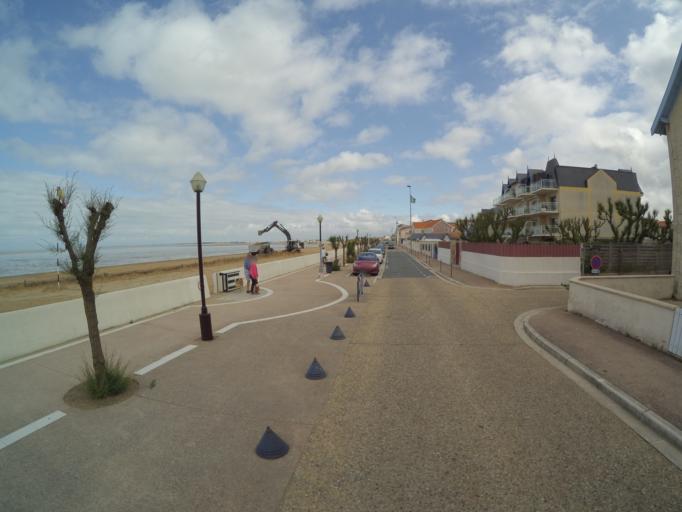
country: FR
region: Poitou-Charentes
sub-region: Departement de la Charente-Maritime
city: Chatelaillon-Plage
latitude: 46.0732
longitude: -1.0932
